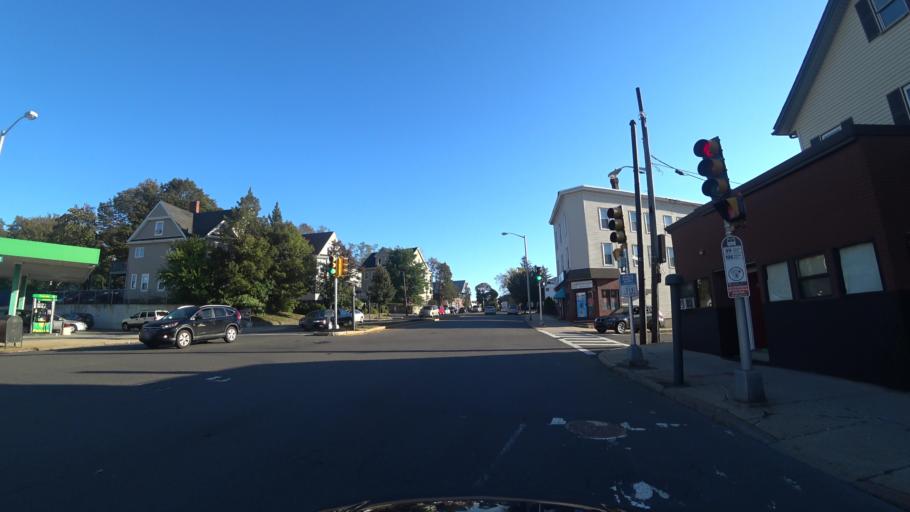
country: US
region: Massachusetts
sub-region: Middlesex County
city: Malden
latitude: 42.4234
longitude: -71.0674
